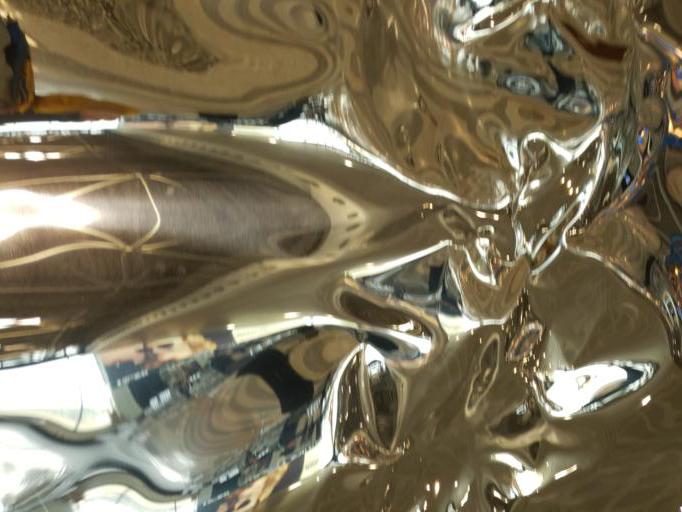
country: IT
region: Lombardy
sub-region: Provincia di Varese
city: Vizzola Ticino
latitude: 45.6289
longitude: 8.7124
